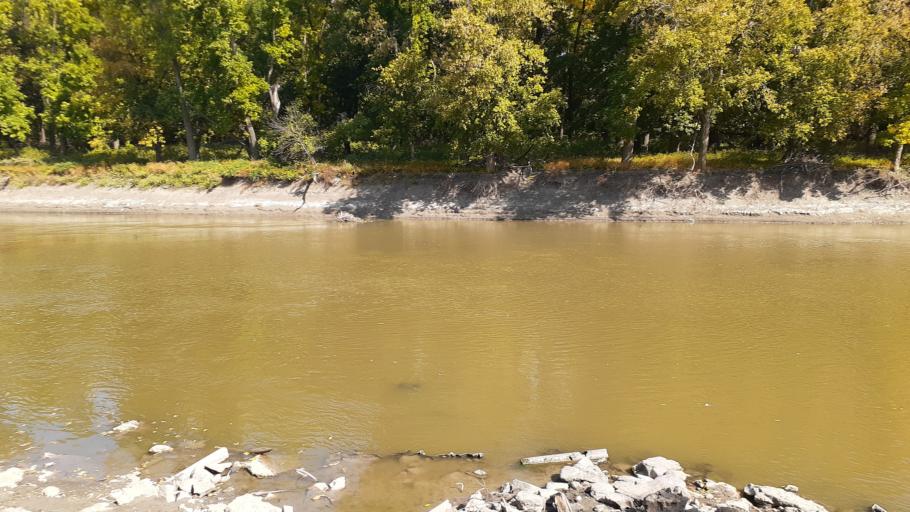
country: US
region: Minnesota
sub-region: Clay County
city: Oakport
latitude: 46.9198
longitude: -96.7622
